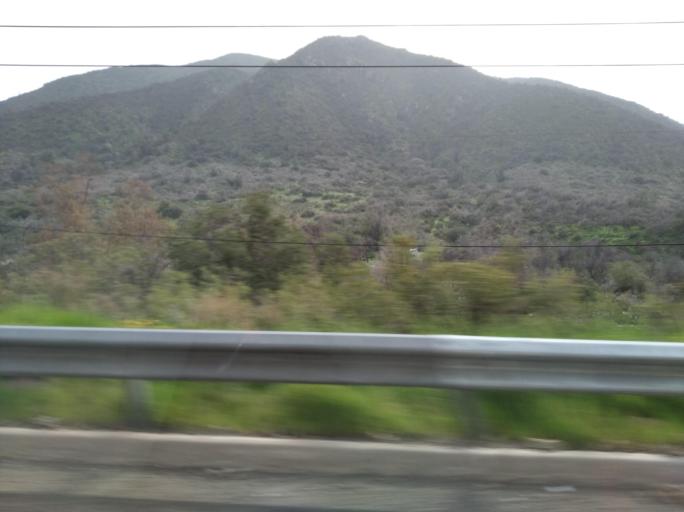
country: CL
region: Santiago Metropolitan
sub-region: Provincia de Chacabuco
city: Lampa
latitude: -33.0768
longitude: -70.9533
